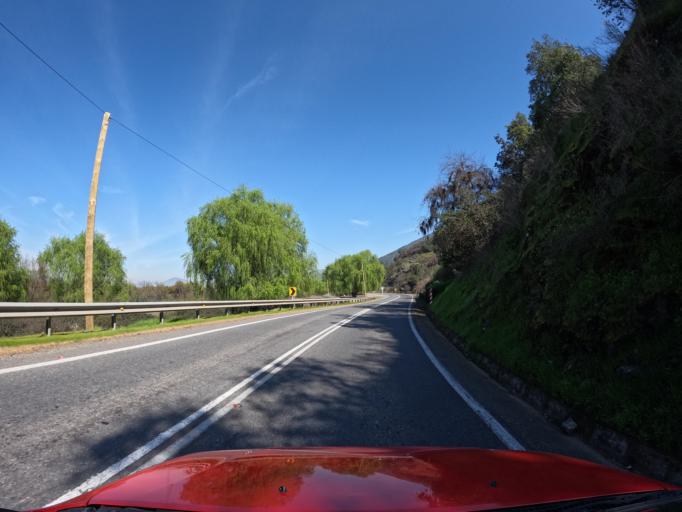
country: CL
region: Maule
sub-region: Provincia de Curico
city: Rauco
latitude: -34.9897
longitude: -71.4308
